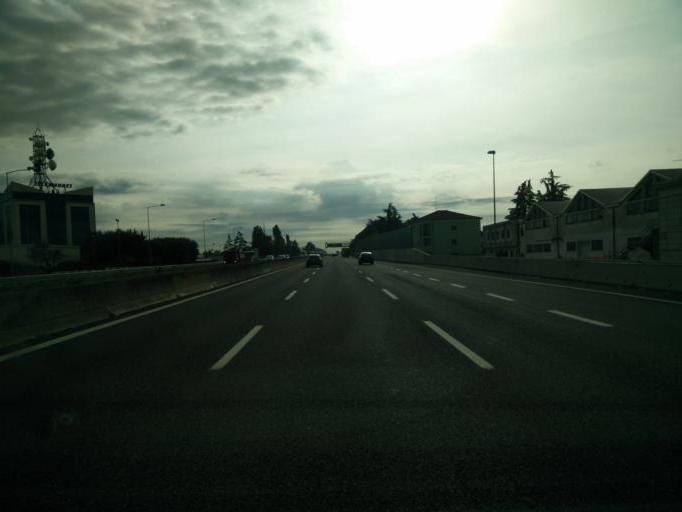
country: IT
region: Lombardy
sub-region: Provincia di Brescia
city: Roncadelle
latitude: 45.5311
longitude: 10.1527
